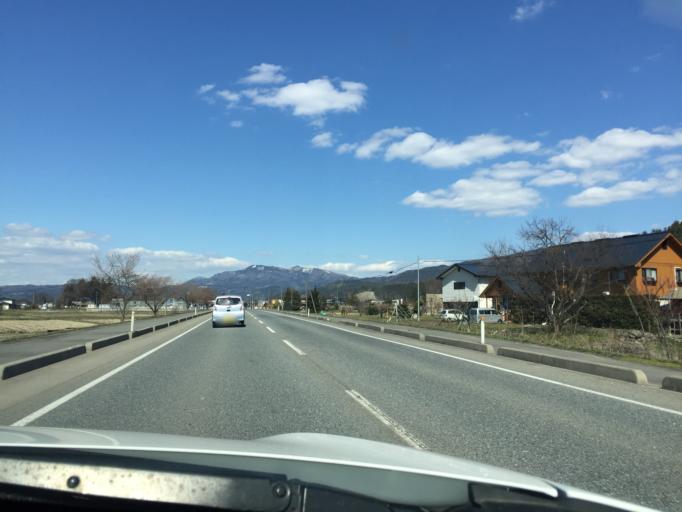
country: JP
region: Yamagata
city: Nagai
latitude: 38.1544
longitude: 140.0678
